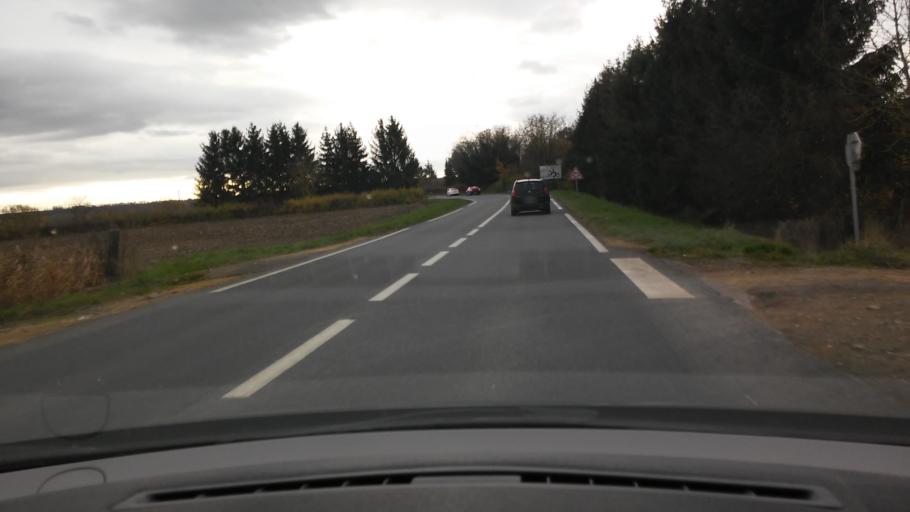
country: FR
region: Lorraine
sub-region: Departement de la Moselle
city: Argancy
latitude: 49.1751
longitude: 6.2143
